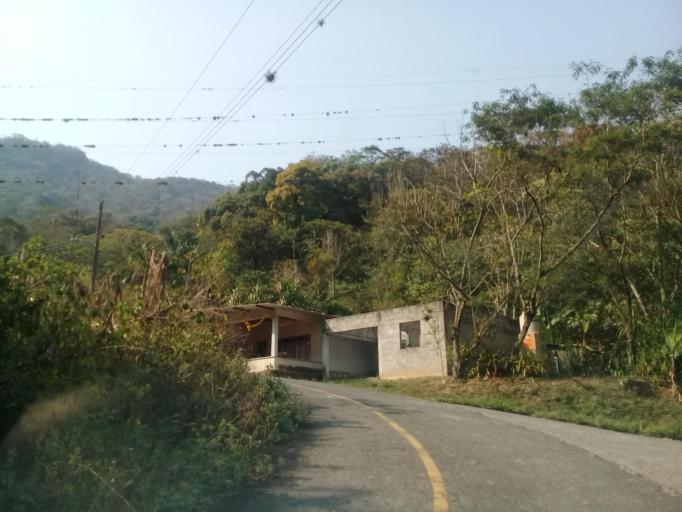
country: MX
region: Veracruz
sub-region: Ixtaczoquitlan
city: Campo Chico
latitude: 18.8363
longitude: -97.0364
